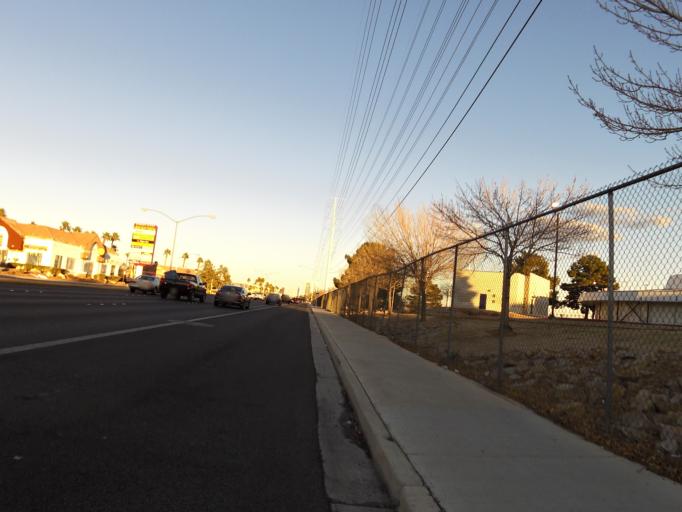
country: US
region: Nevada
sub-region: Clark County
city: Spring Valley
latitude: 36.1144
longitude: -115.2329
